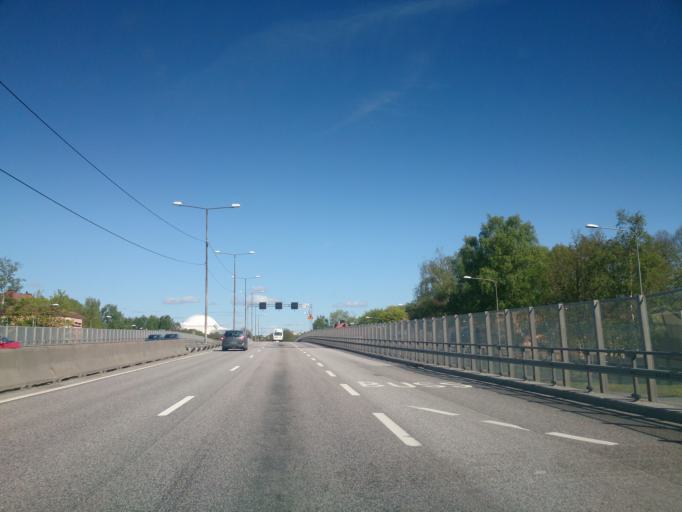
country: SE
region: Stockholm
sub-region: Stockholms Kommun
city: Arsta
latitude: 59.2780
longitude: 18.0924
